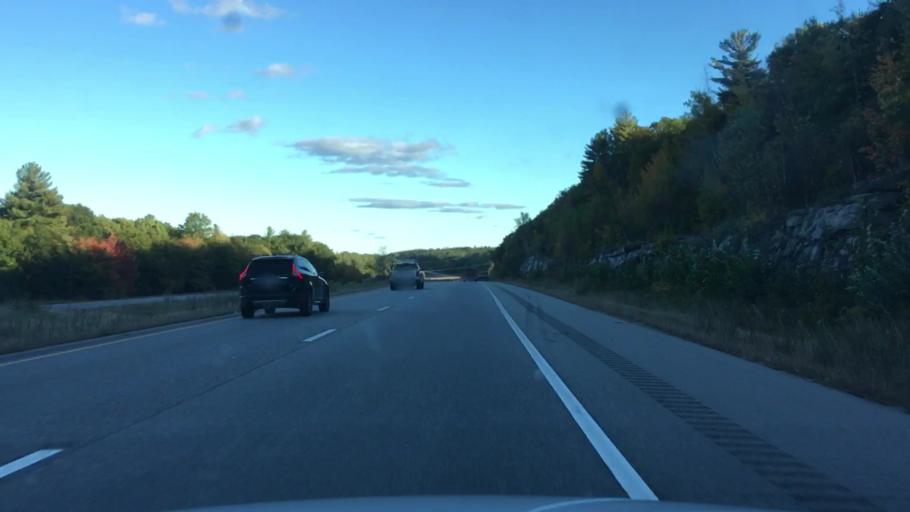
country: US
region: New Hampshire
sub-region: Rockingham County
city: Candia
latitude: 43.0395
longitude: -71.2635
